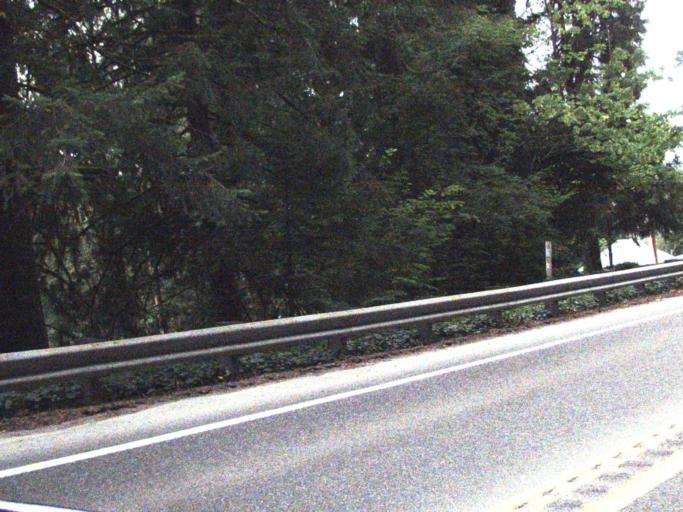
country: US
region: Washington
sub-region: King County
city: Snoqualmie
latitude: 47.5540
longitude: -121.8390
